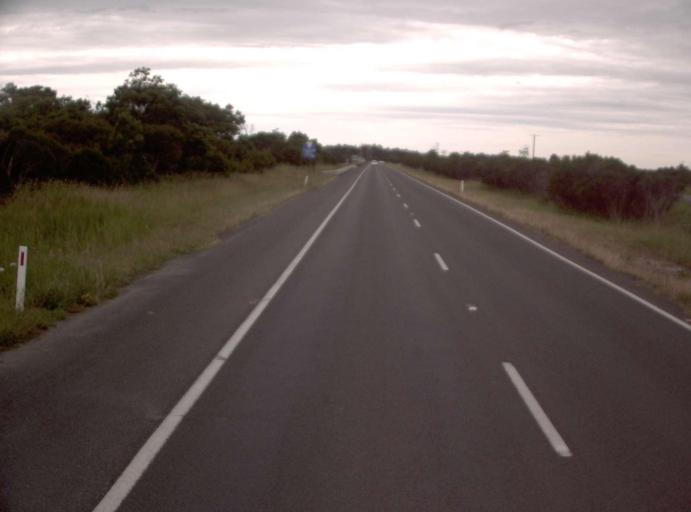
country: AU
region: Victoria
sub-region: Cardinia
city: Koo-Wee-Rup
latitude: -38.2132
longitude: 145.4605
